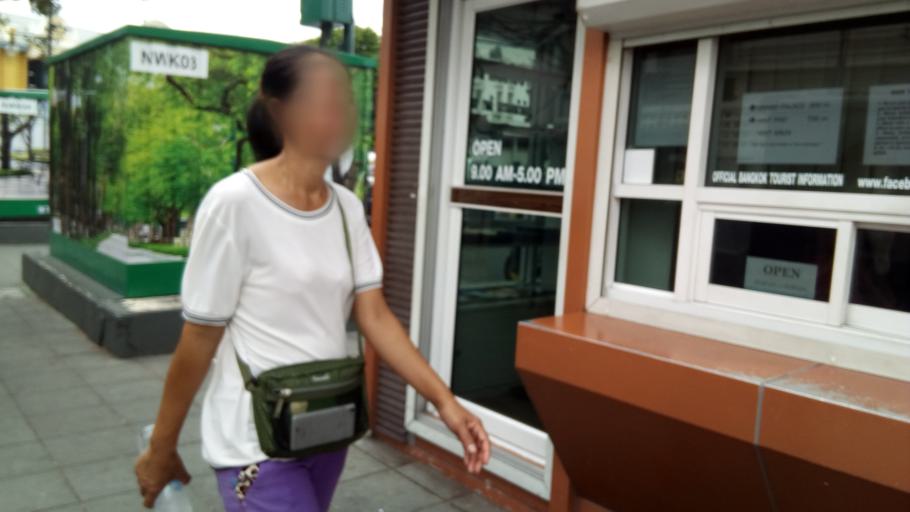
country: TH
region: Bangkok
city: Bangkok
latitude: 13.7519
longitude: 100.4893
